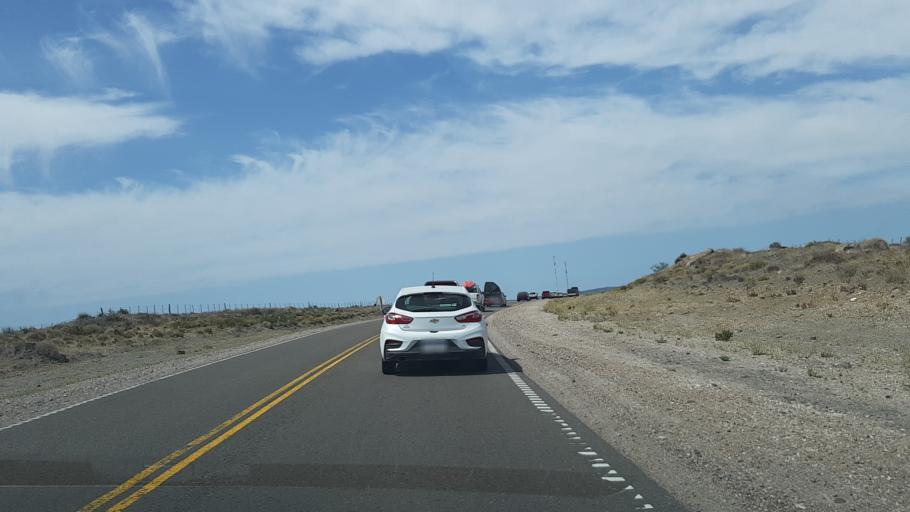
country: AR
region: Neuquen
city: Piedra del Aguila
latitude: -39.9882
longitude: -70.0396
